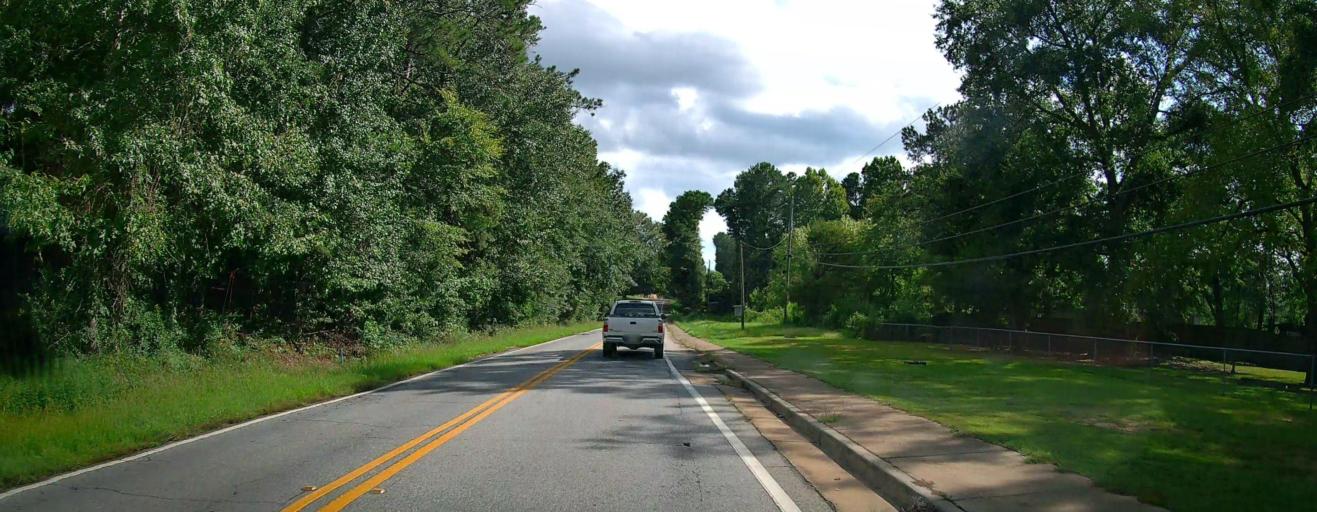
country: US
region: Alabama
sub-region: Russell County
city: Phenix City
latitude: 32.5682
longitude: -84.9694
